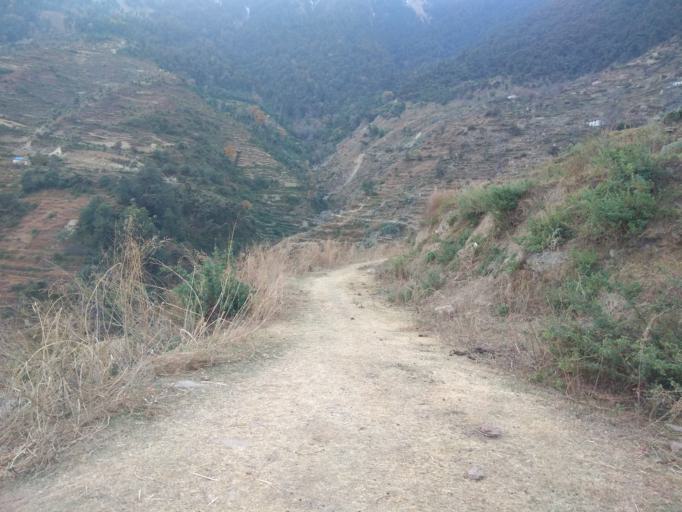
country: NP
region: Mid Western
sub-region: Karnali Zone
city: Jumla
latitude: 29.3246
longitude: 81.7226
